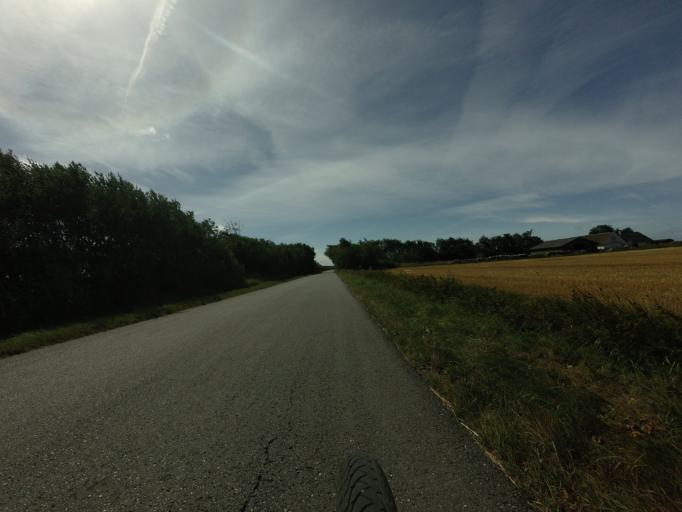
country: DK
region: North Denmark
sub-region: Bronderslev Kommune
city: Bronderslev
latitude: 57.3203
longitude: 9.8153
